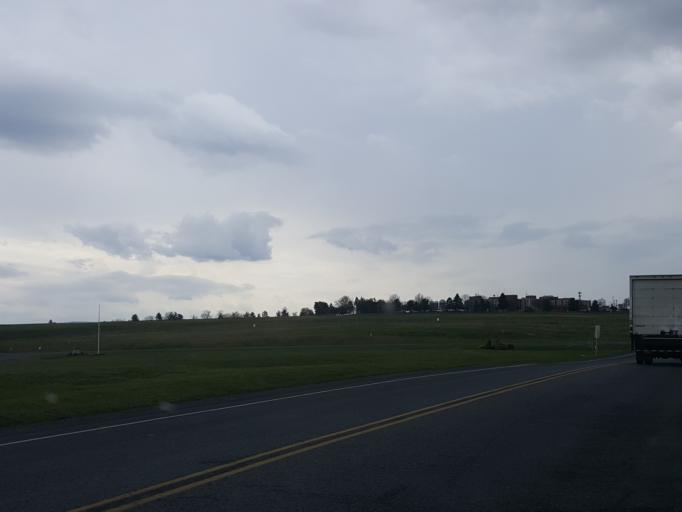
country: US
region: Pennsylvania
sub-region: Berks County
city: Fox Chase
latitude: 40.3877
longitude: -75.9779
